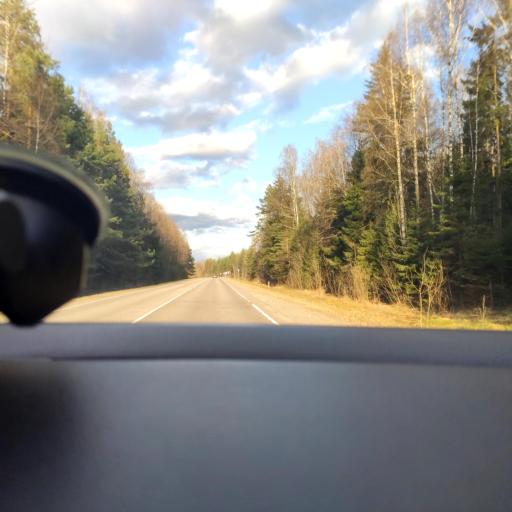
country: RU
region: Moskovskaya
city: Shaturtorf
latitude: 55.4297
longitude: 39.3813
